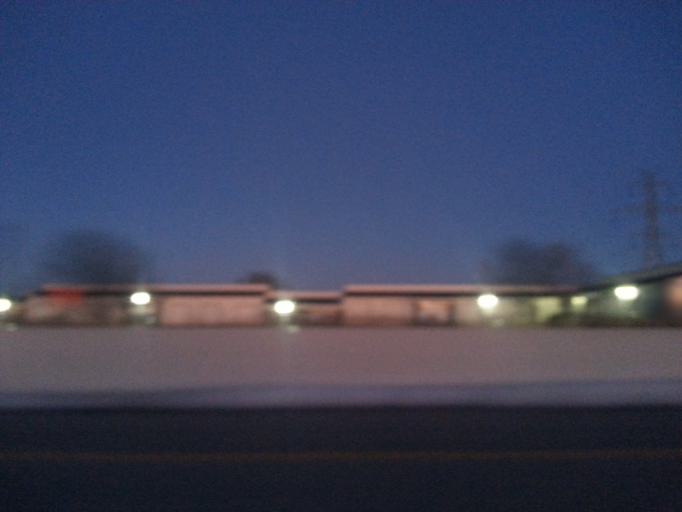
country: US
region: Indiana
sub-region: Lake County
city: Merrillville
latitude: 41.4606
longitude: -87.3227
